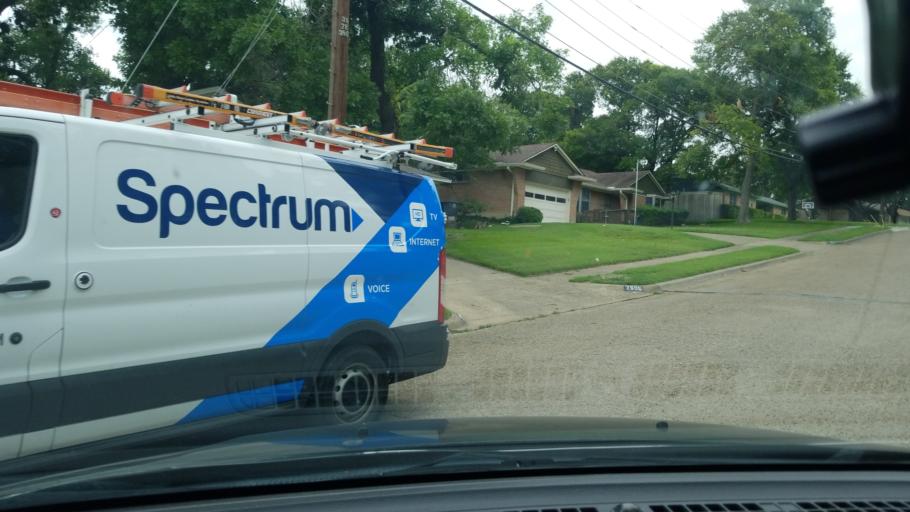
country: US
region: Texas
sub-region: Dallas County
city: Highland Park
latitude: 32.8134
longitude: -96.6972
